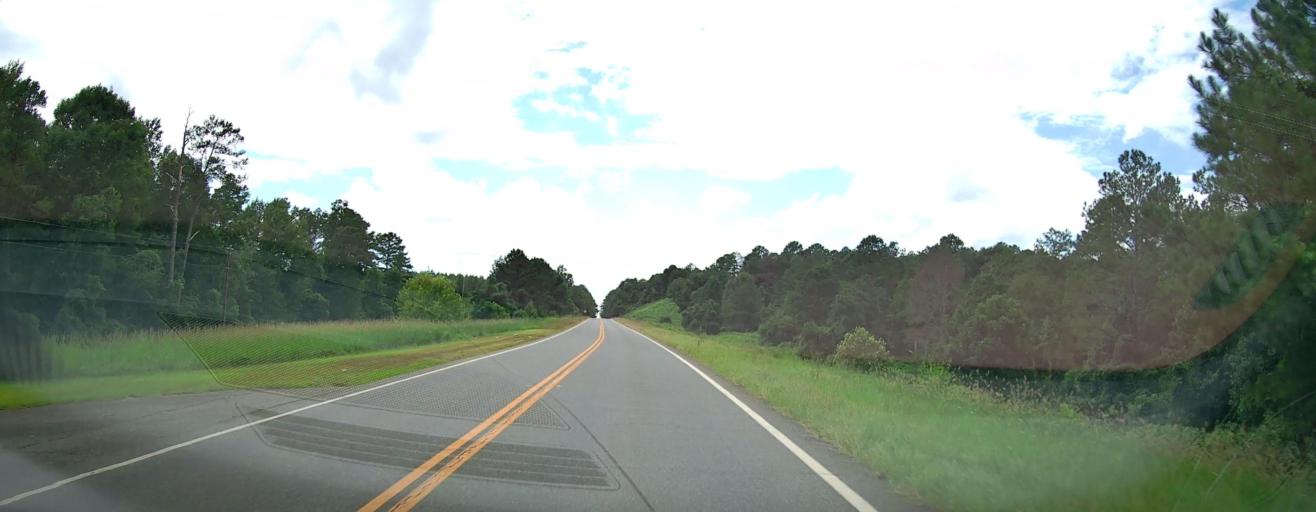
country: US
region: Georgia
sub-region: Marion County
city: Buena Vista
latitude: 32.3191
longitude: -84.5488
